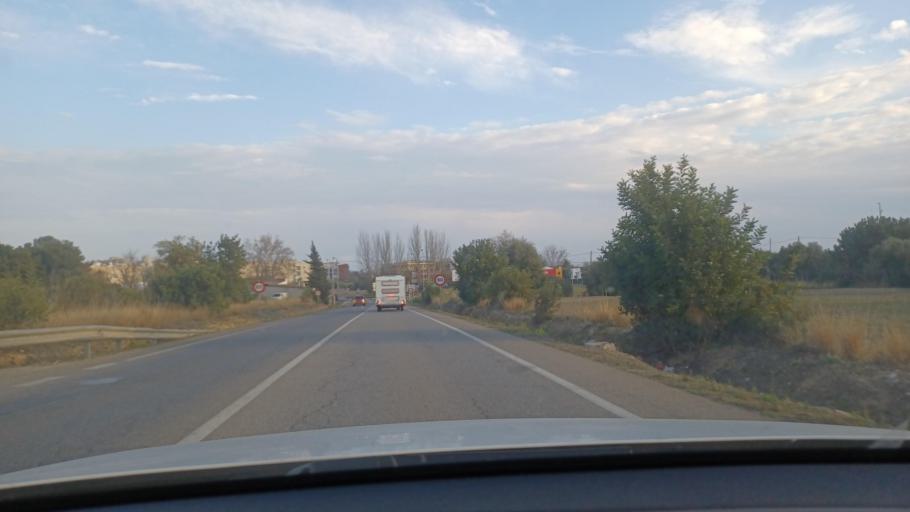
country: ES
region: Catalonia
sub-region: Provincia de Tarragona
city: Cambrils
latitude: 41.0717
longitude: 1.0477
